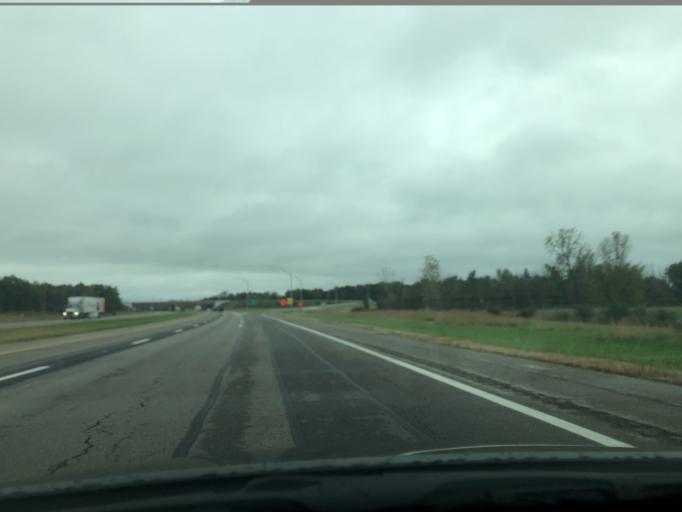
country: US
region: Ohio
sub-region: Champaign County
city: North Lewisburg
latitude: 40.3210
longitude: -83.5819
